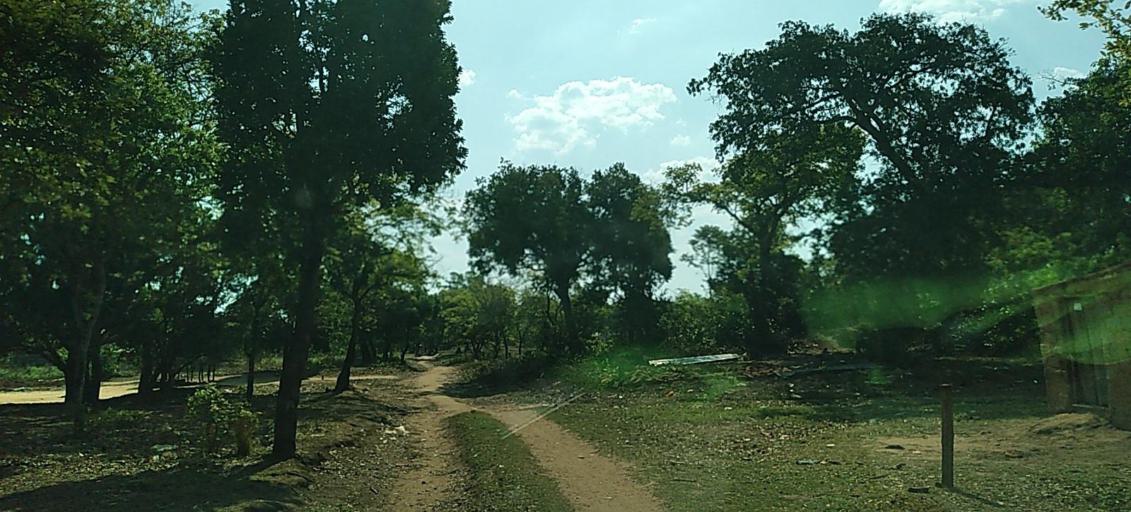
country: ZM
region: North-Western
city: Mwinilunga
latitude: -11.2979
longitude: 24.8562
